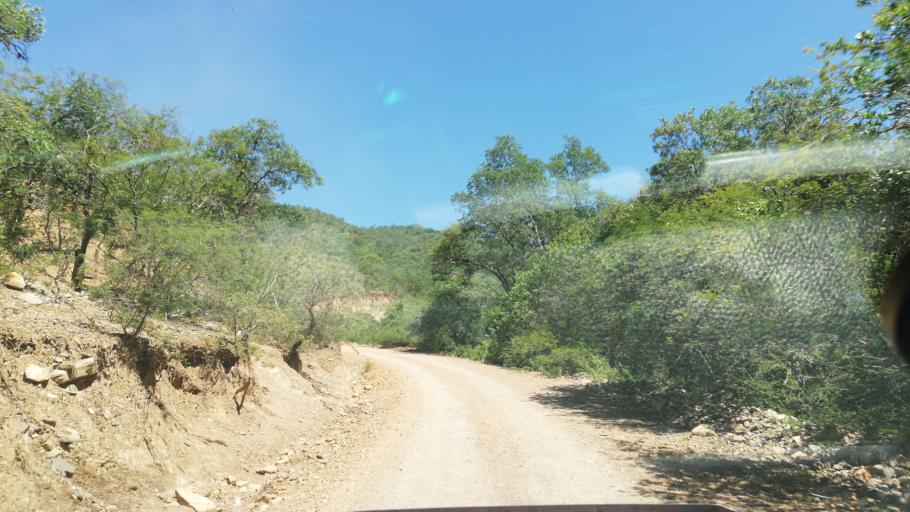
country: BO
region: Cochabamba
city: Mizque
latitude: -17.8902
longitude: -65.2795
